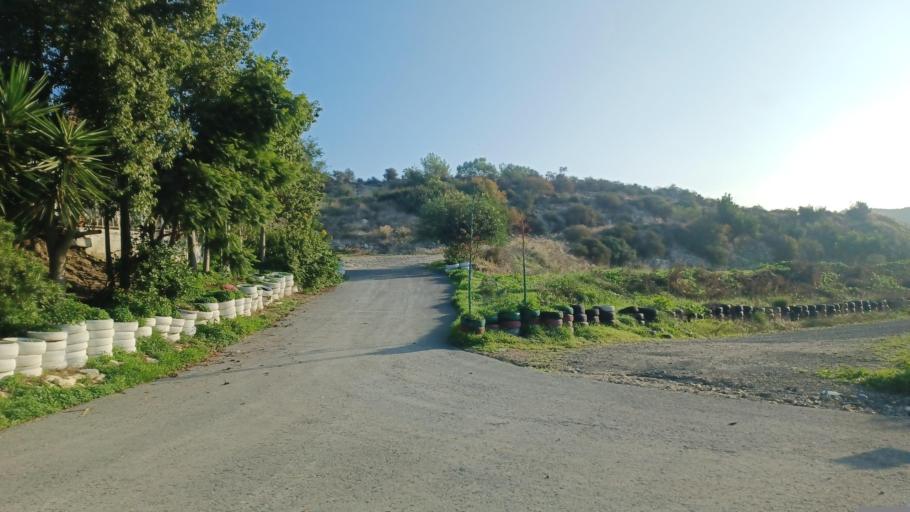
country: CY
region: Larnaka
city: Kofinou
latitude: 34.8138
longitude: 33.3233
